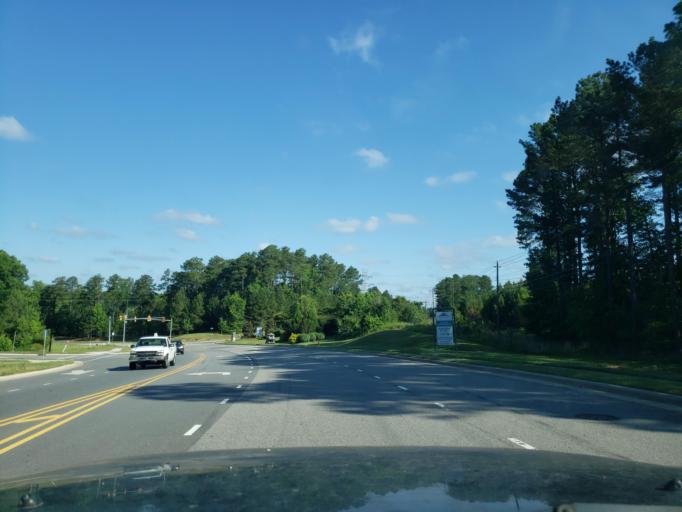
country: US
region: North Carolina
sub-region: Durham County
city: Durham
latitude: 35.9426
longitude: -78.8659
